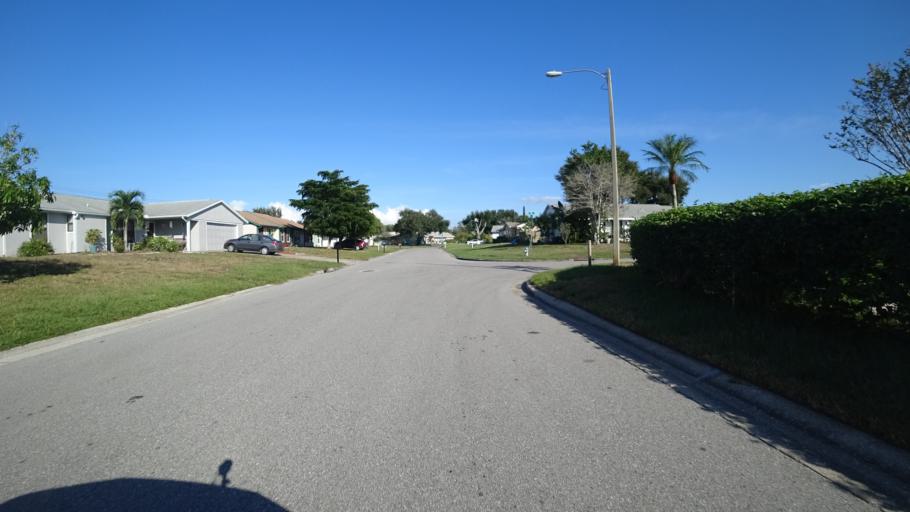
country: US
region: Florida
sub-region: Manatee County
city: West Bradenton
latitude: 27.4733
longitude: -82.6260
